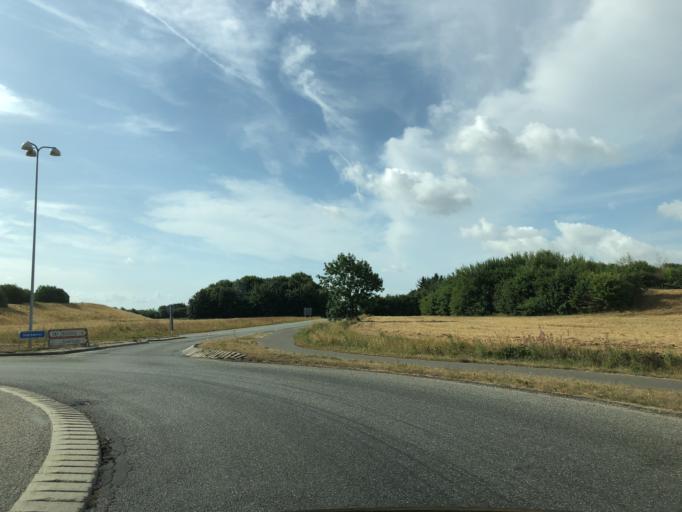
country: DK
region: South Denmark
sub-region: Fredericia Kommune
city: Taulov
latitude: 55.5355
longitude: 9.6374
